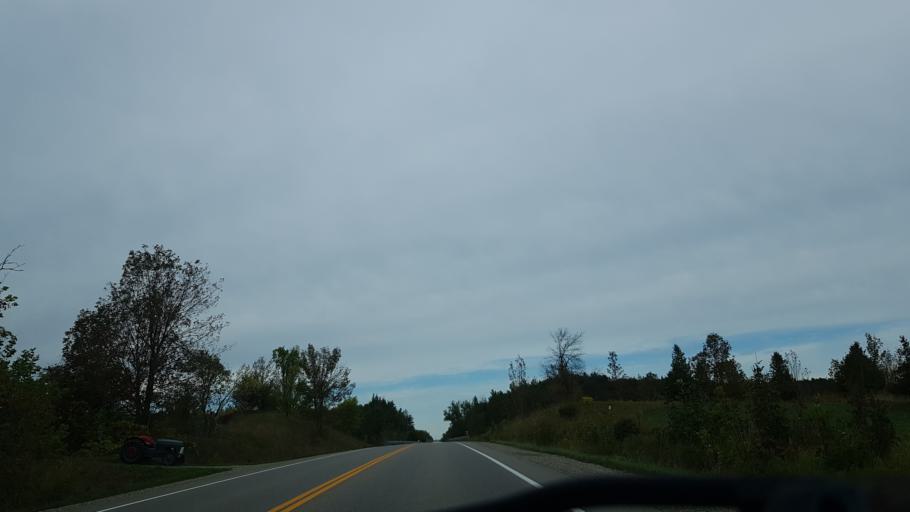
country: CA
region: Ontario
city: Orangeville
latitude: 44.0446
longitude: -80.0100
